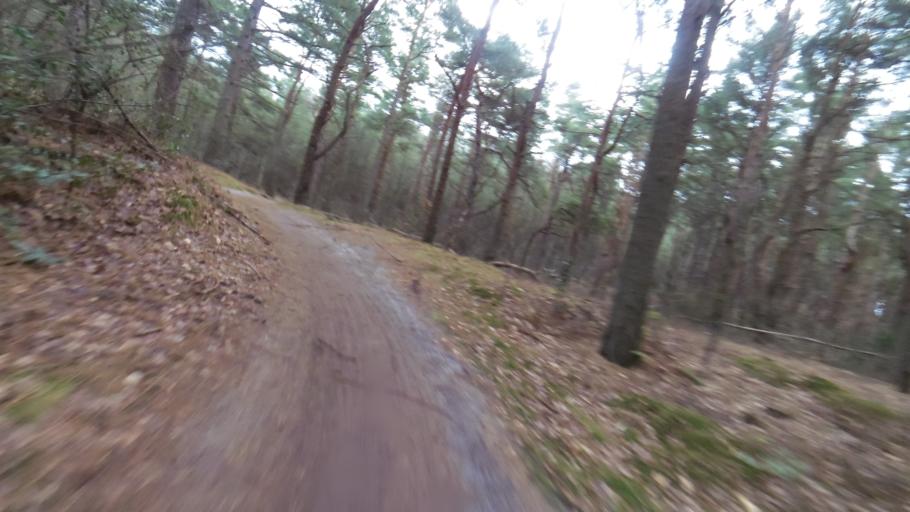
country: NL
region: North Holland
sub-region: Gemeente Heiloo
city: Heiloo
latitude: 52.6844
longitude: 4.6853
